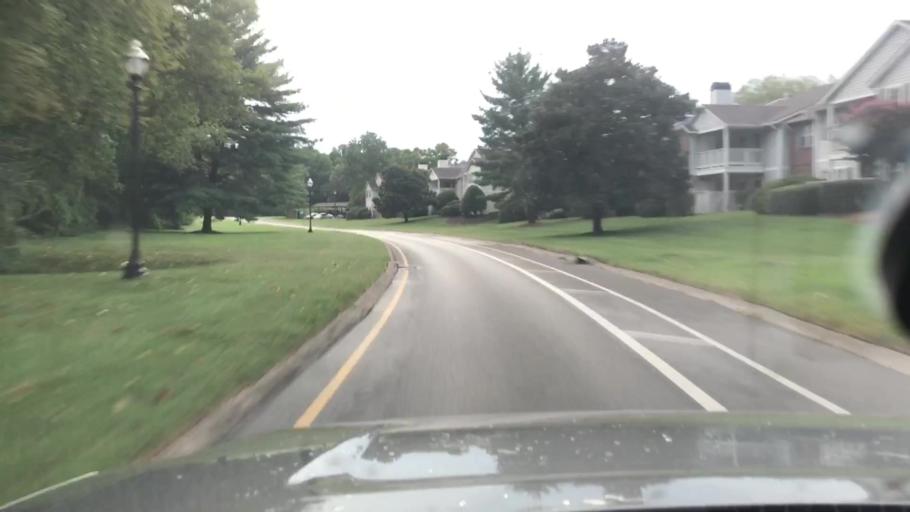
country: US
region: Tennessee
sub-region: Rutherford County
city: La Vergne
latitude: 36.0900
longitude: -86.6403
